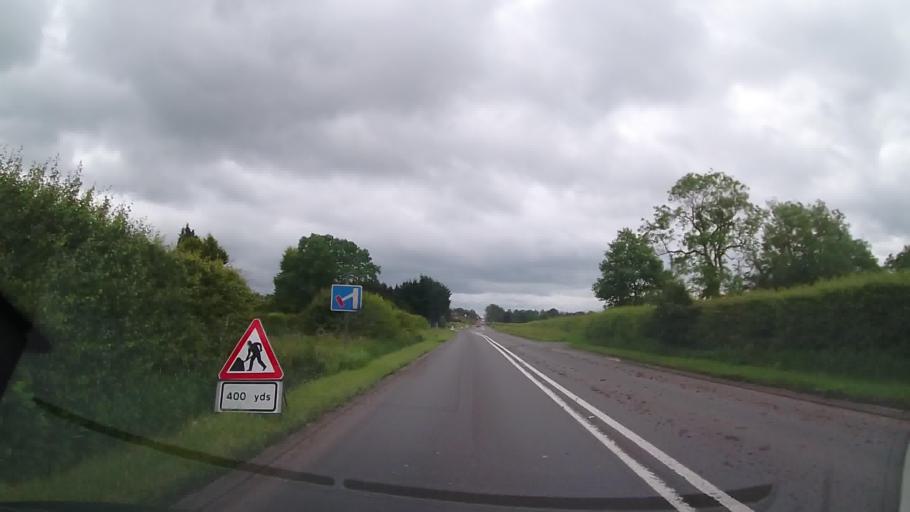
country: GB
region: England
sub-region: Shropshire
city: Stoke upon Tern
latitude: 52.8919
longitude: -2.5516
